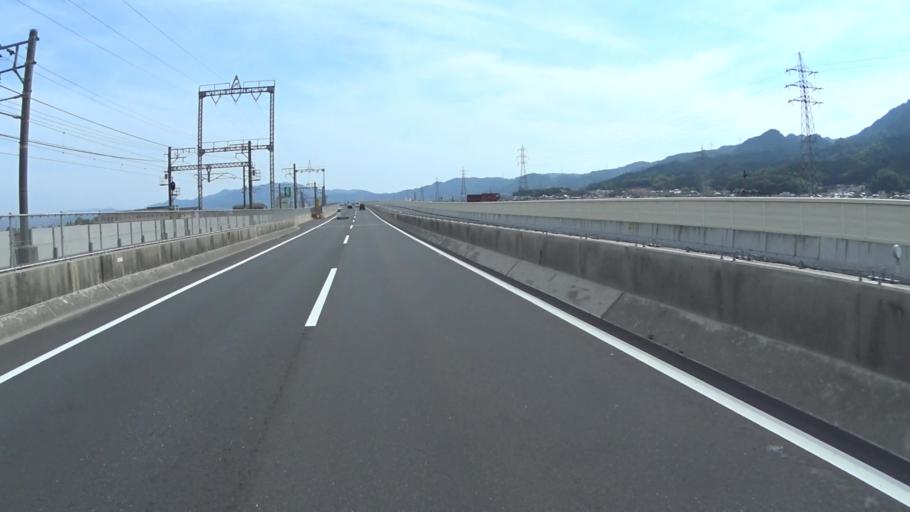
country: JP
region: Shiga Prefecture
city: Otsu-shi
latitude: 35.0672
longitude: 135.8765
